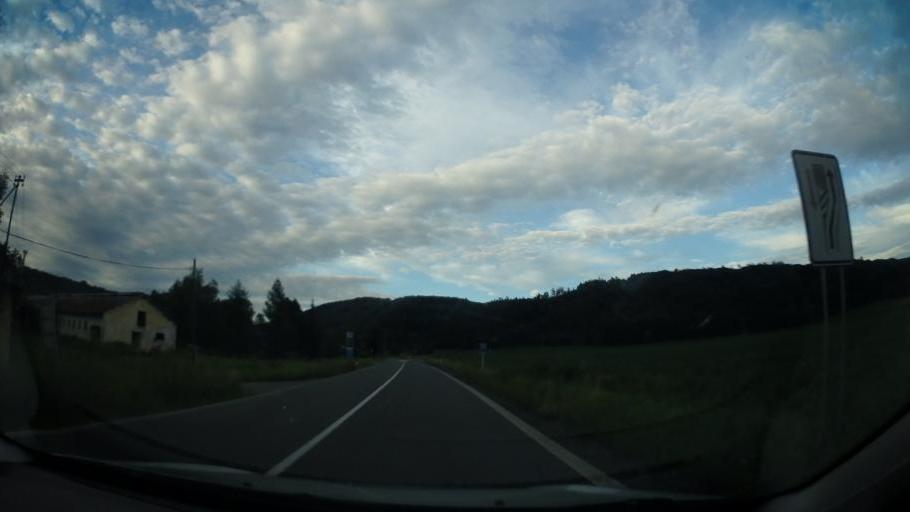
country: CZ
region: Olomoucky
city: Paseka
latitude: 49.8211
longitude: 17.2018
